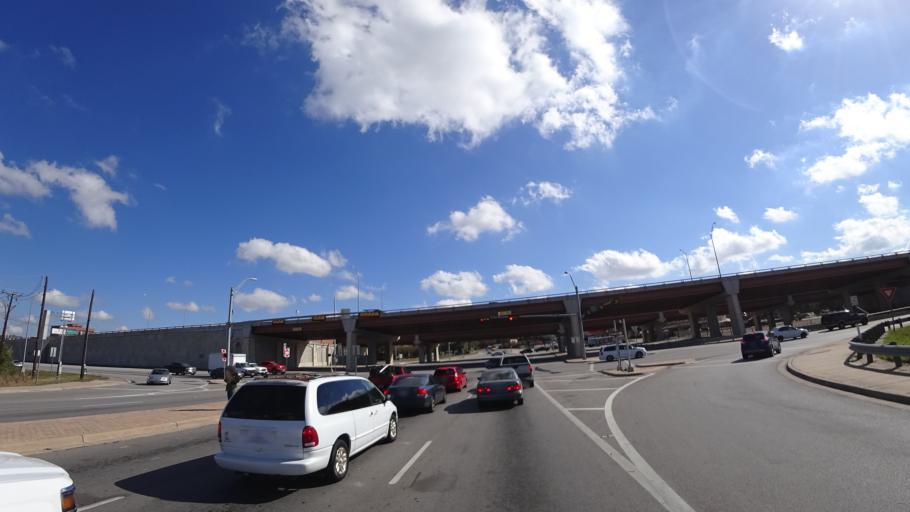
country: US
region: Texas
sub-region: Travis County
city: Wells Branch
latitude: 30.4404
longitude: -97.6992
